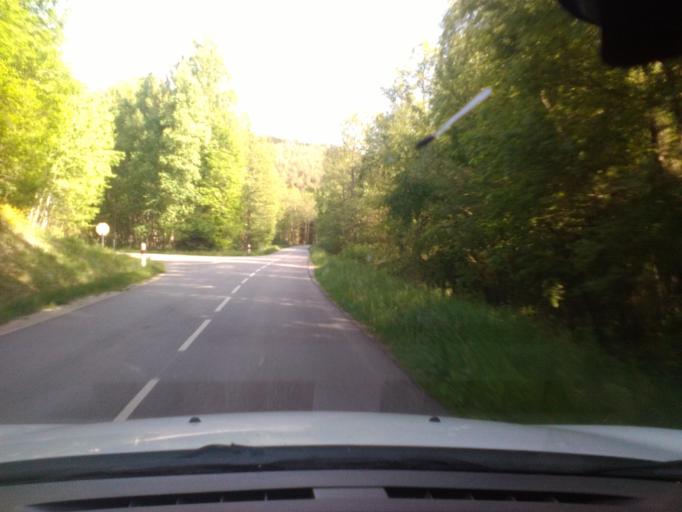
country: FR
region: Lorraine
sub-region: Departement des Vosges
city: Bruyeres
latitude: 48.2678
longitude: 6.7240
